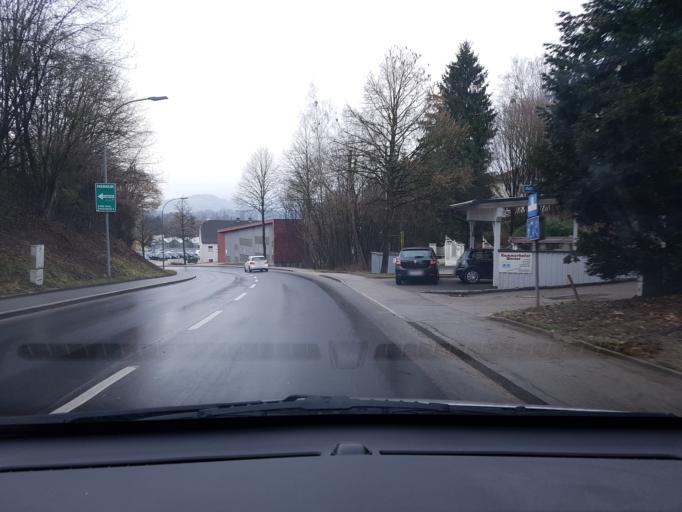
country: AT
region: Upper Austria
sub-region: Steyr Stadt
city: Steyr
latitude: 48.0475
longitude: 14.4101
